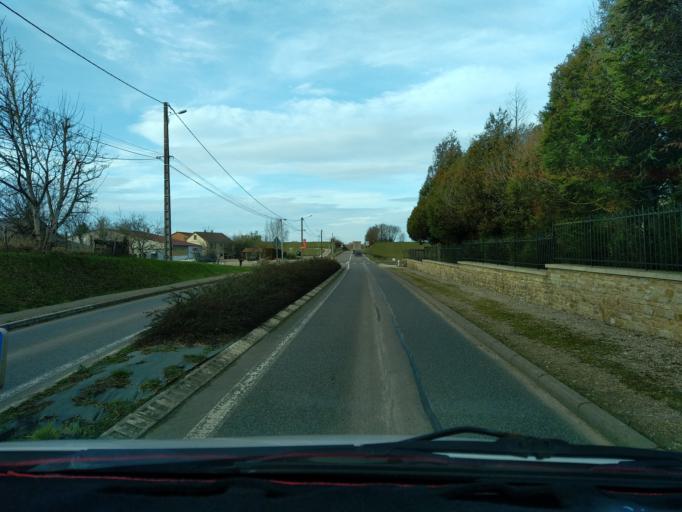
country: FR
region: Franche-Comte
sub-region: Departement de la Haute-Saone
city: Gray
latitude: 47.3618
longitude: 5.6738
